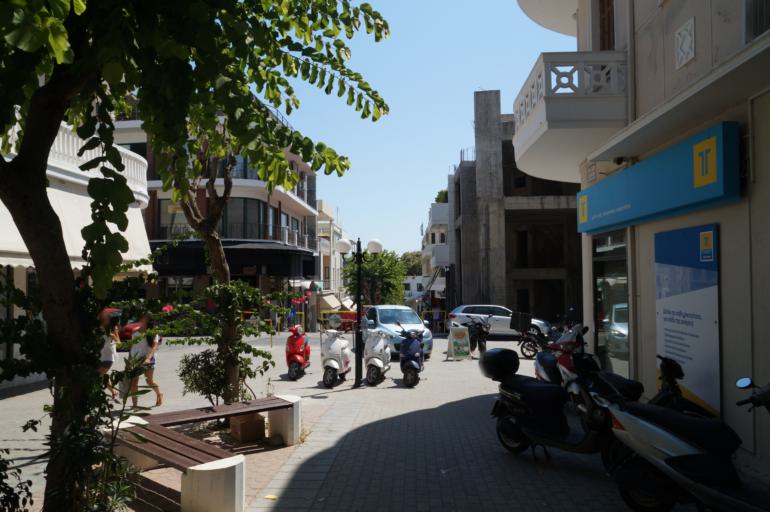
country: GR
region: South Aegean
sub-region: Nomos Dodekanisou
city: Rodos
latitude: 36.4478
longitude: 28.2239
